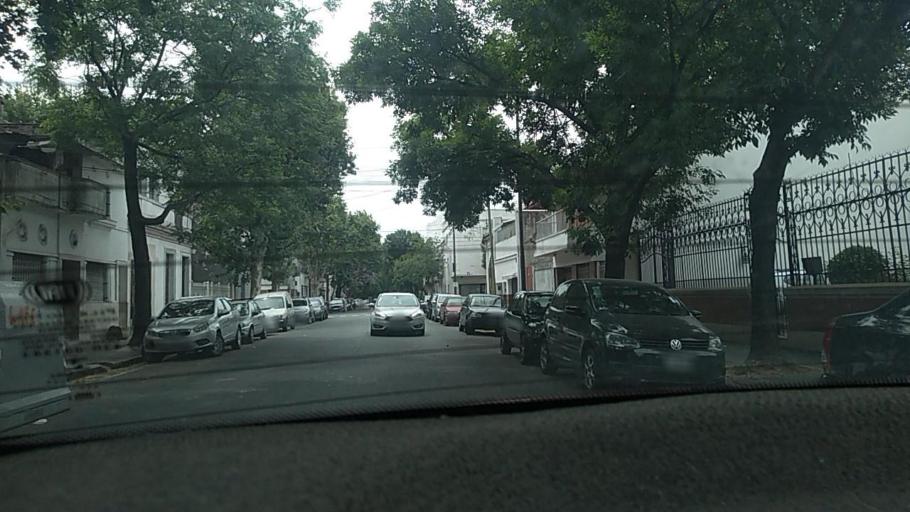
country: AR
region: Buenos Aires F.D.
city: Villa Santa Rita
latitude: -34.6373
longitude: -58.4747
